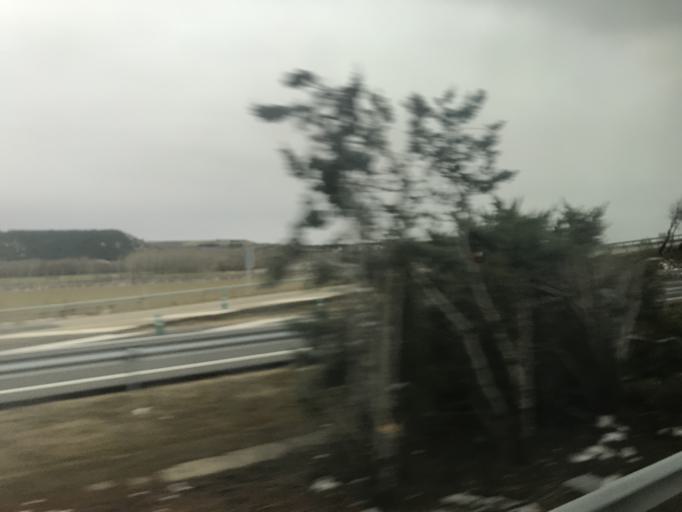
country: ES
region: Castille and Leon
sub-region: Provincia de Burgos
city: Villaldemiro
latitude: 42.2379
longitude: -3.9786
